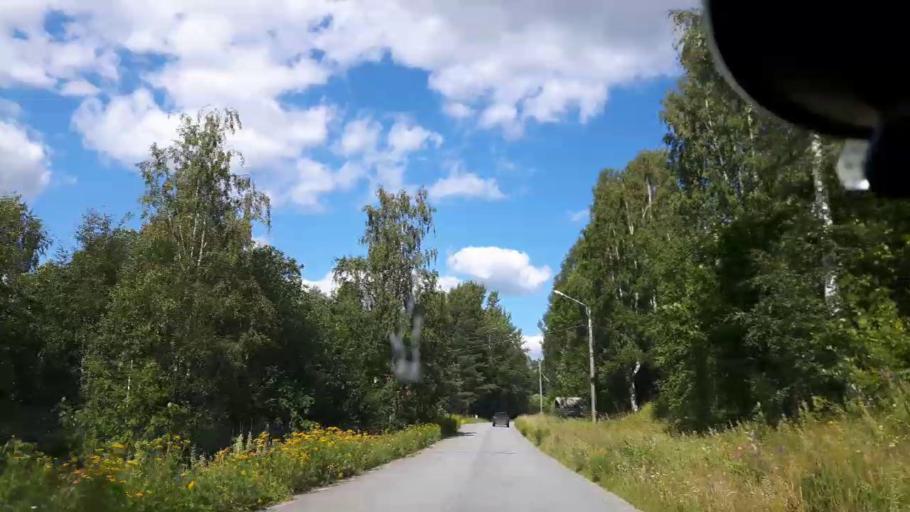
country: SE
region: Jaemtland
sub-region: Ragunda Kommun
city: Hammarstrand
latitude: 62.9486
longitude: 16.6884
